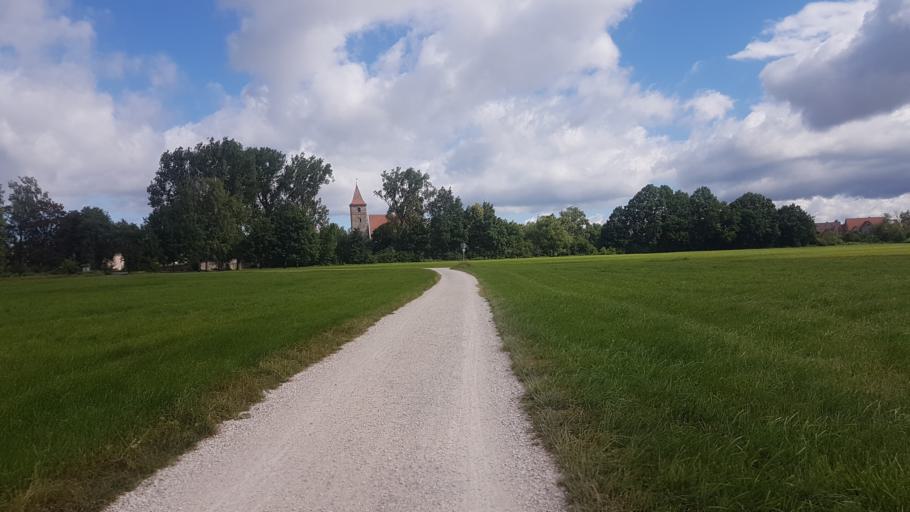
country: DE
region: Bavaria
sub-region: Regierungsbezirk Mittelfranken
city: Ornbau
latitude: 49.1718
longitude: 10.6564
